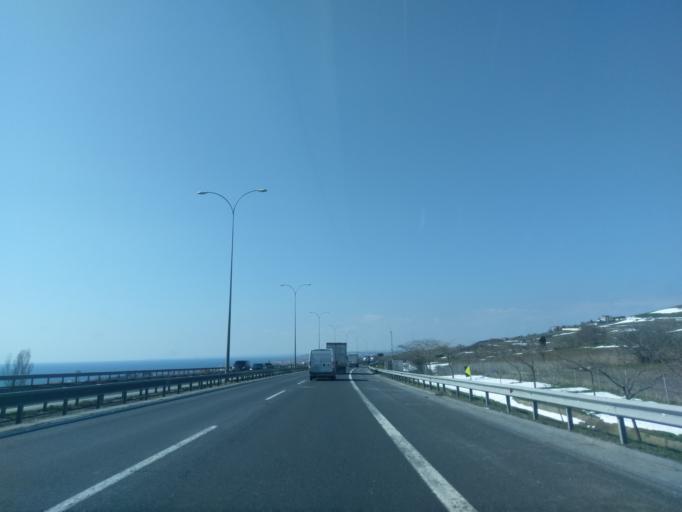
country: TR
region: Istanbul
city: Celaliye
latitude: 41.0509
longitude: 28.4392
